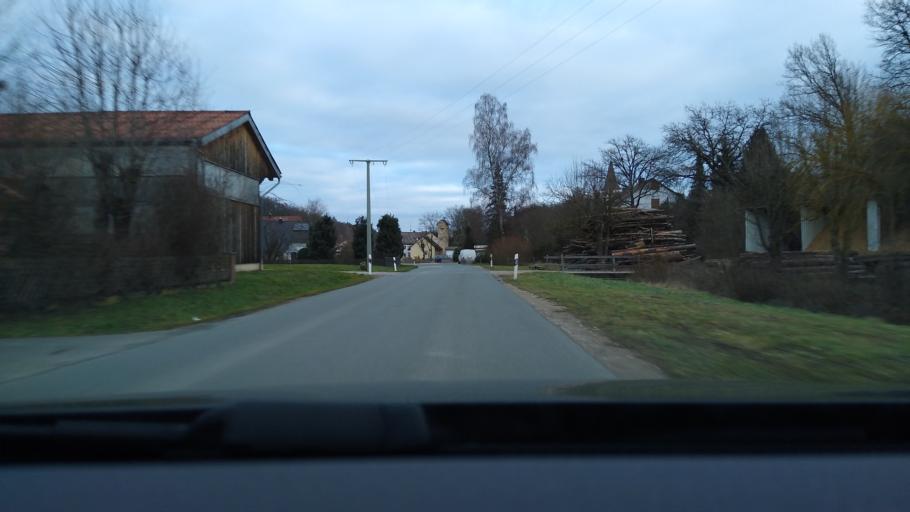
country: DE
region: Bavaria
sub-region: Regierungsbezirk Mittelfranken
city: Schwabach
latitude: 49.3684
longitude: 10.9971
